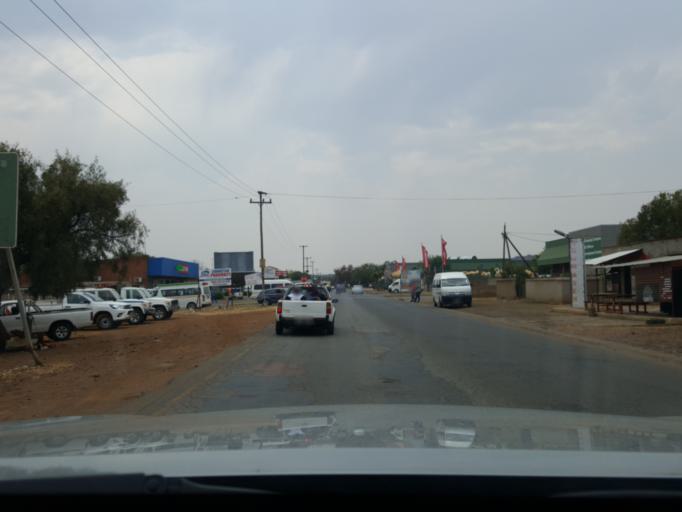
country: ZA
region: North-West
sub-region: Ngaka Modiri Molema District Municipality
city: Zeerust
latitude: -25.4951
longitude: 25.9841
